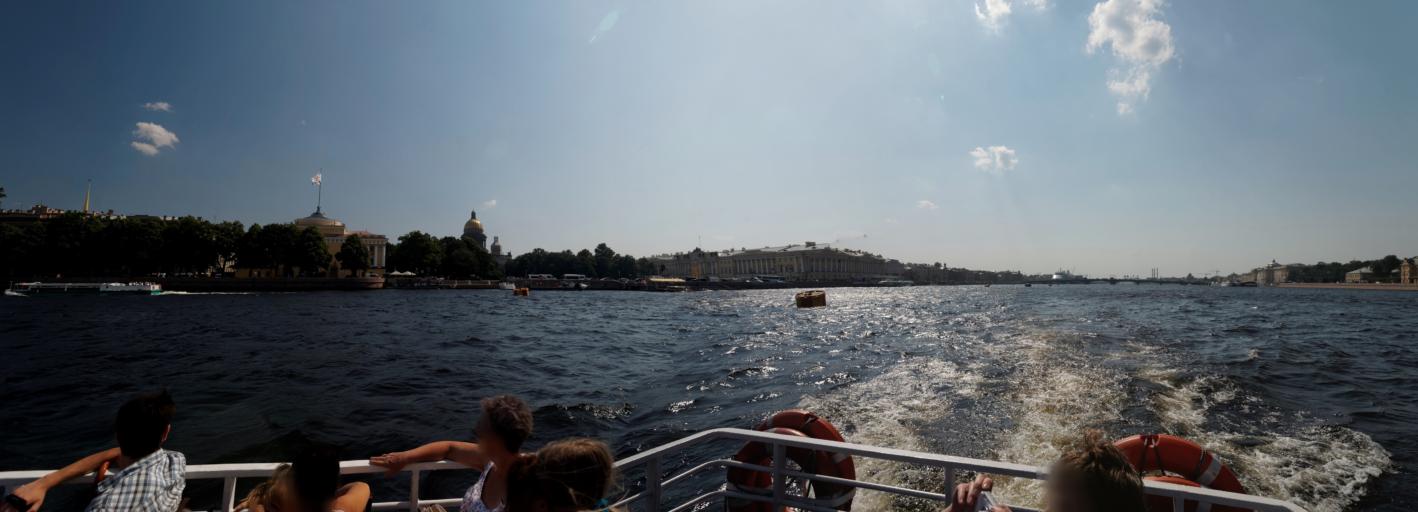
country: RU
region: St.-Petersburg
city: Saint Petersburg
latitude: 59.9381
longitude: 30.3024
